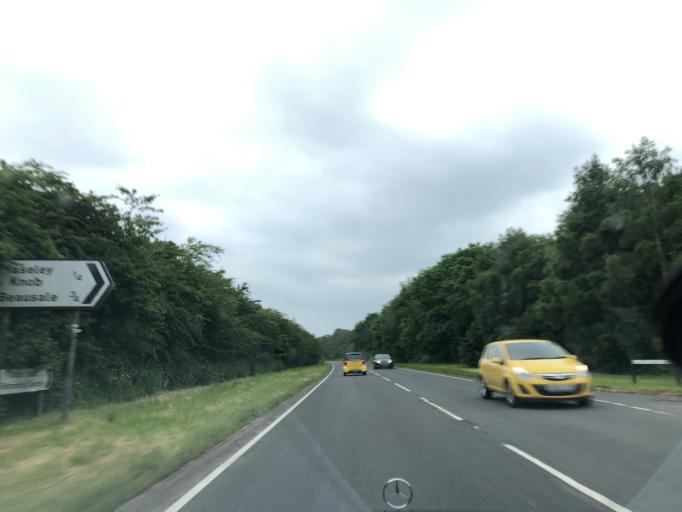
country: GB
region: England
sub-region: Warwickshire
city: Wroxall
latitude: 52.3449
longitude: -1.6543
